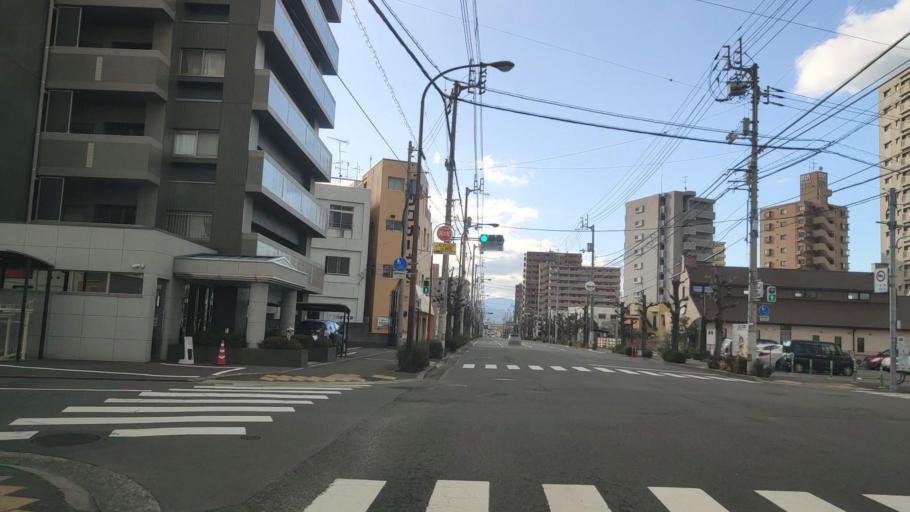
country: JP
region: Ehime
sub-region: Shikoku-chuo Shi
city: Matsuyama
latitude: 33.8347
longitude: 132.7525
